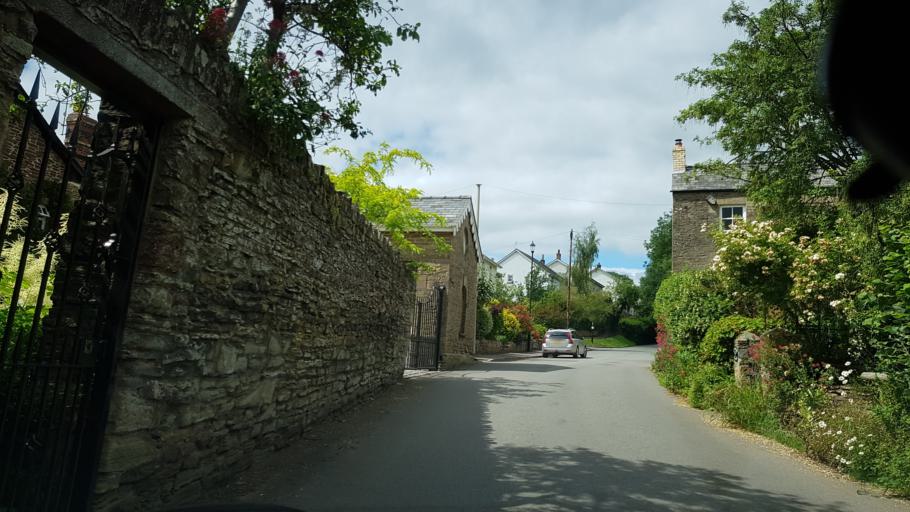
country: GB
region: Wales
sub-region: Monmouthshire
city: Grosmont
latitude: 51.9154
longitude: -2.8679
